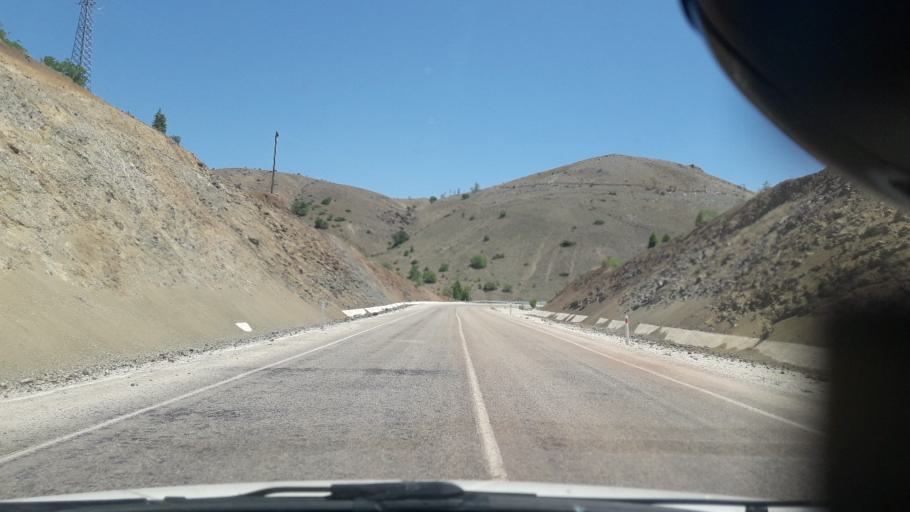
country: TR
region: Malatya
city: Hekimhan
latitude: 38.8298
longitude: 37.8666
